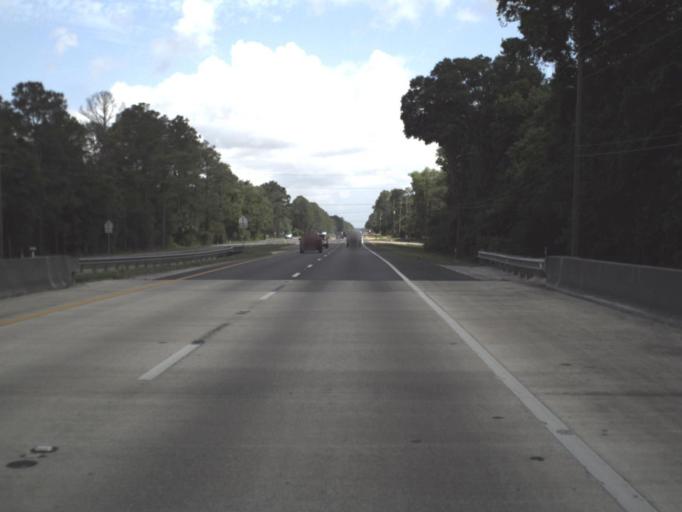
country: US
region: Florida
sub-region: Saint Johns County
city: Saint Augustine Shores
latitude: 29.7746
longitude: -81.3158
